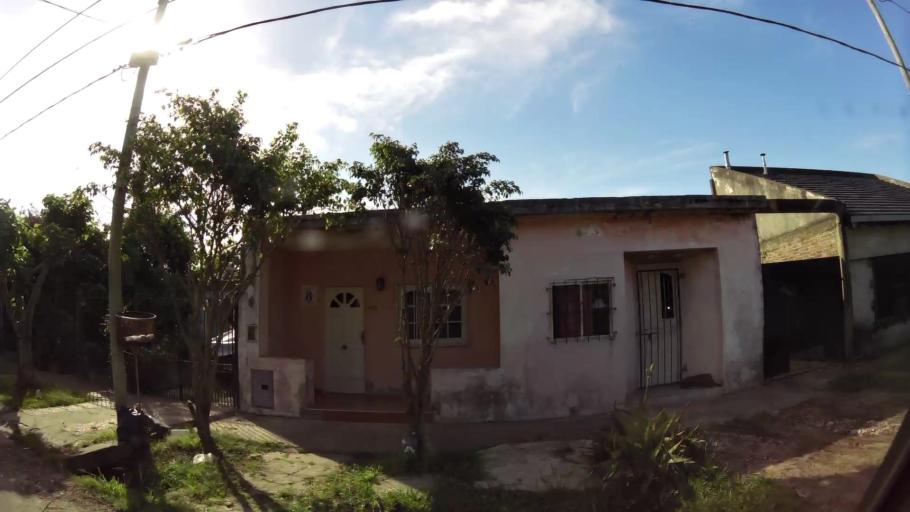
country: AR
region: Buenos Aires
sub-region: Partido de Quilmes
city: Quilmes
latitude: -34.7932
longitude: -58.2297
